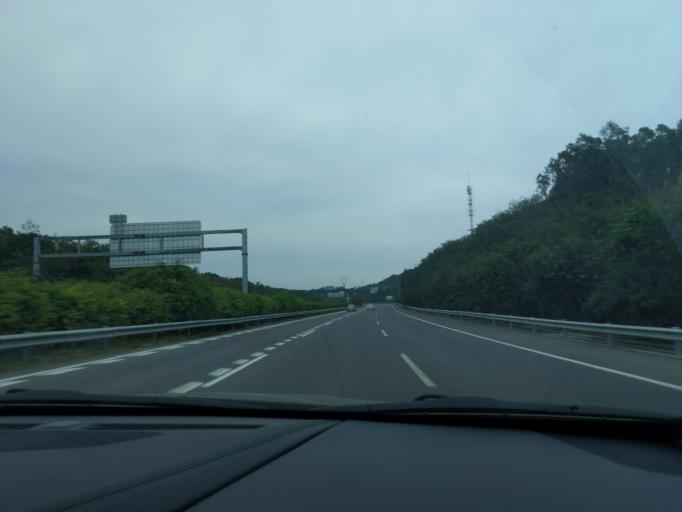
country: CN
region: Fujian
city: Shishi
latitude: 24.7501
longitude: 118.5916
